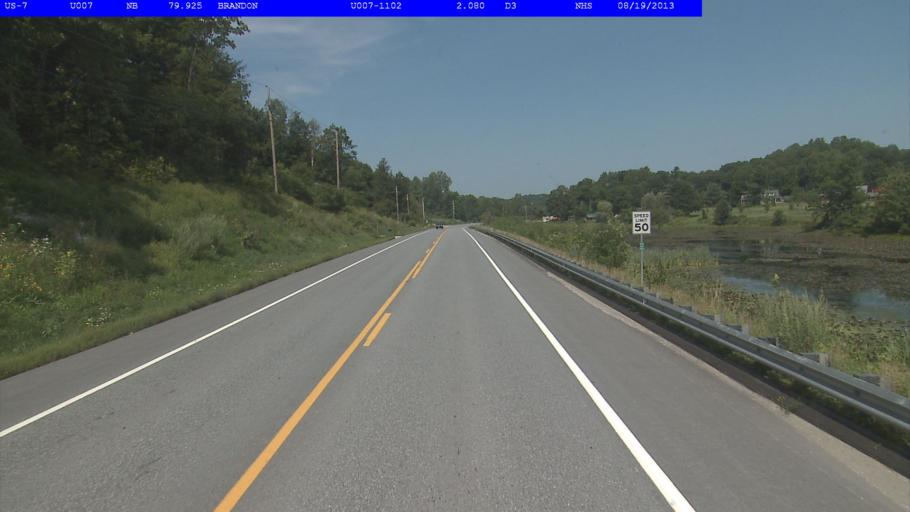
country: US
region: Vermont
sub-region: Rutland County
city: Brandon
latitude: 43.7820
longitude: -73.0610
